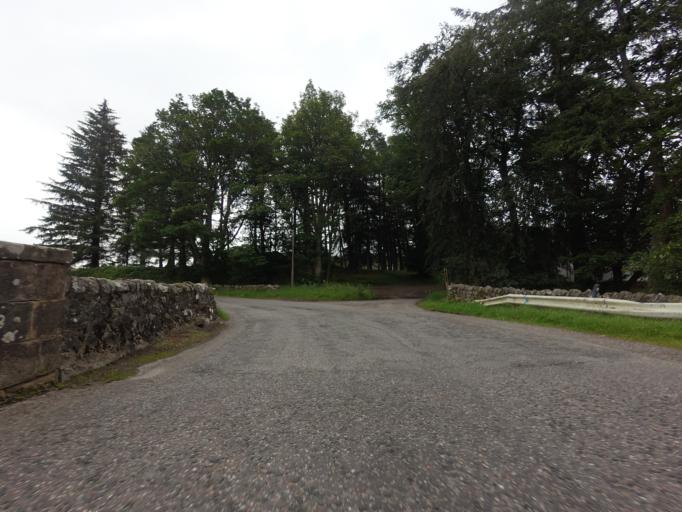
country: GB
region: Scotland
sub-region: Highland
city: Evanton
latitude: 57.8859
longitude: -4.3874
